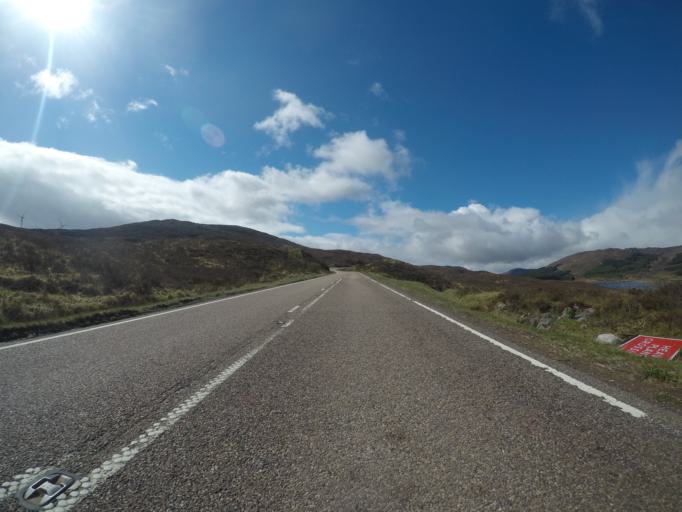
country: GB
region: Scotland
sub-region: Highland
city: Spean Bridge
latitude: 57.1241
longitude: -4.9708
